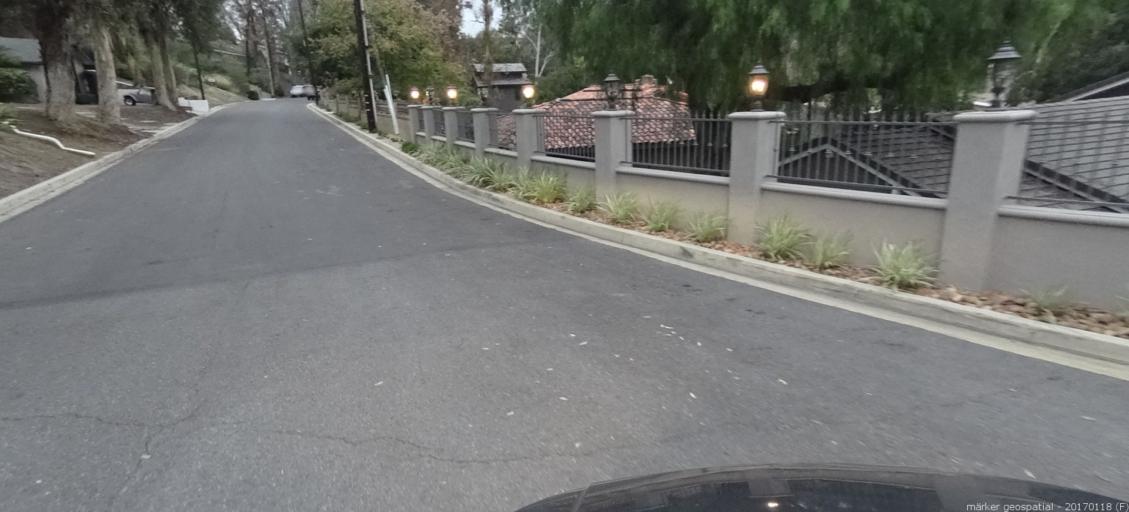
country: US
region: California
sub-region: Orange County
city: North Tustin
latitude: 33.7752
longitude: -117.7642
